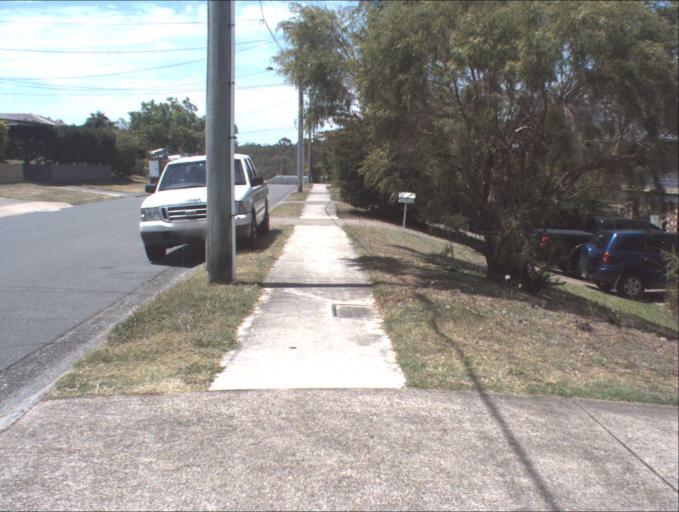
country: AU
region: Queensland
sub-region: Logan
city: Rochedale South
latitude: -27.5973
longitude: 153.1426
